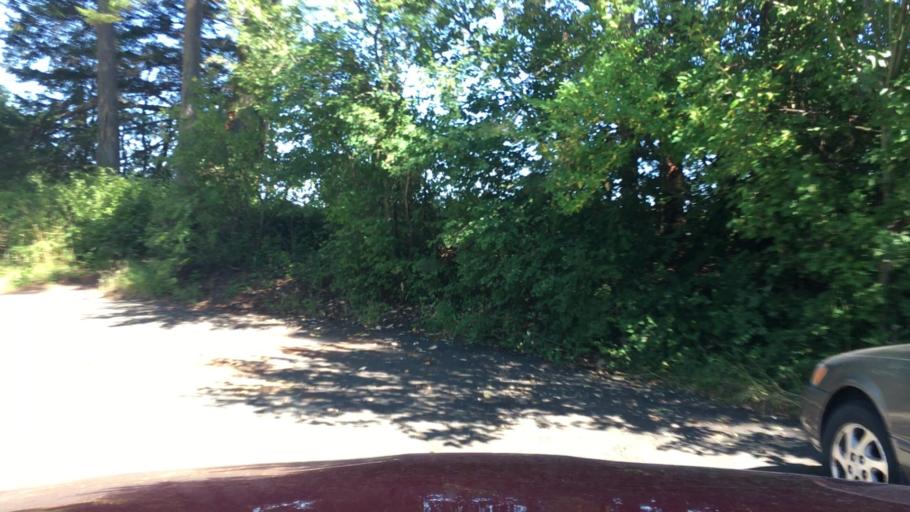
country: CA
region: British Columbia
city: North Saanich
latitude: 48.6752
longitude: -123.4168
